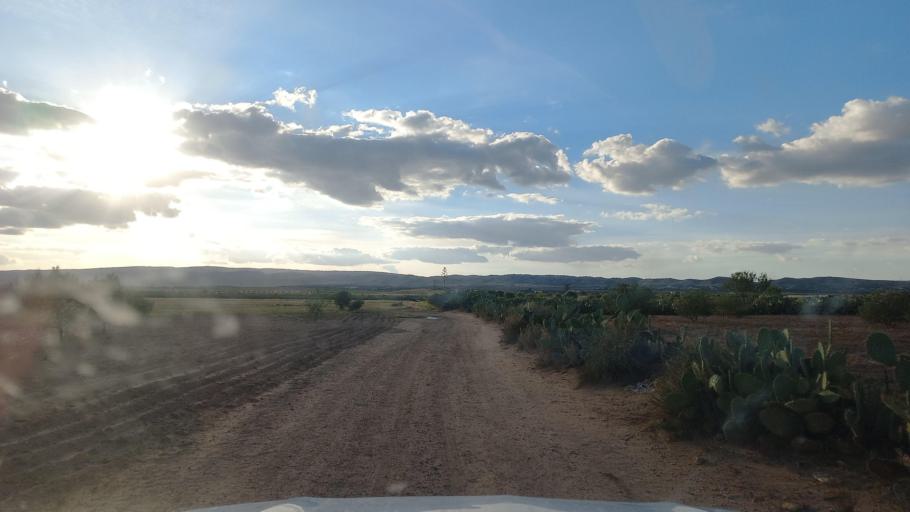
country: TN
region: Al Qasrayn
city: Sbiba
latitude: 35.3520
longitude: 9.0349
